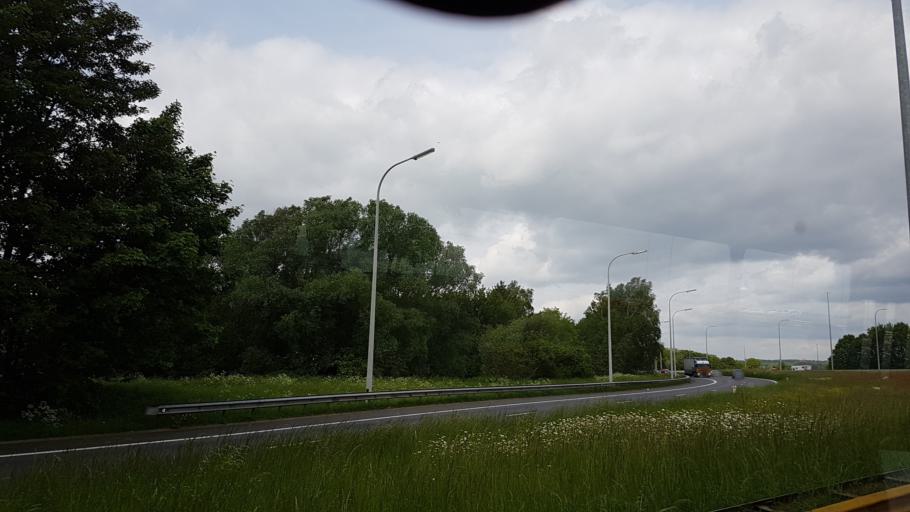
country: BE
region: Flanders
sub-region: Provincie Vlaams-Brabant
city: Bertem
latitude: 50.8560
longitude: 4.6381
